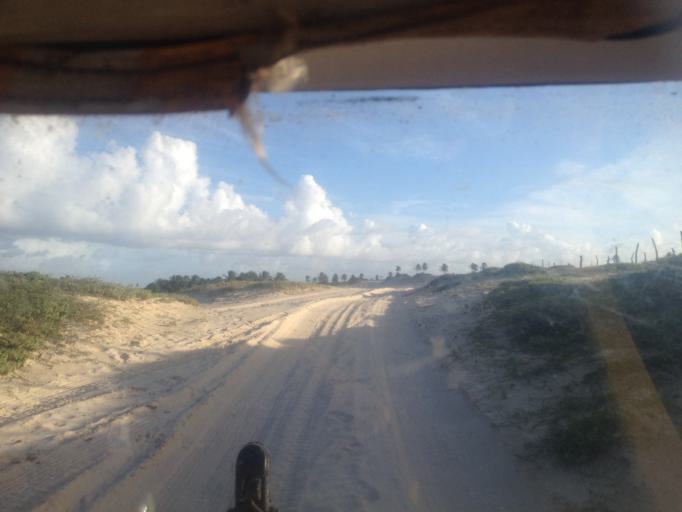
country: BR
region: Sergipe
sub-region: Indiaroba
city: Indiaroba
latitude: -11.4654
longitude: -37.3637
